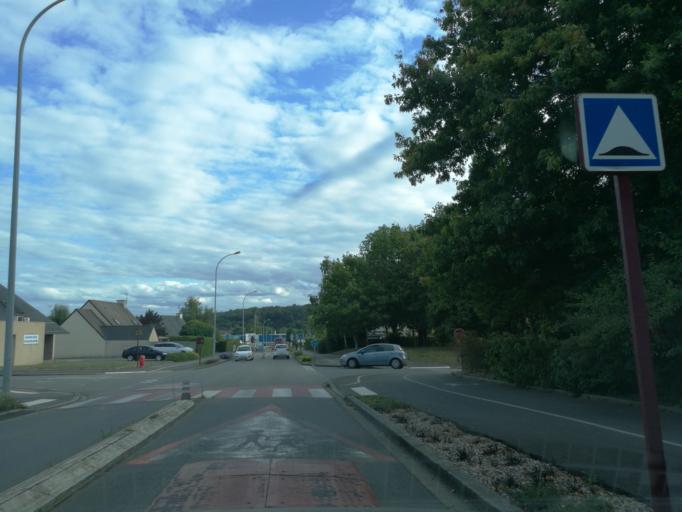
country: FR
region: Brittany
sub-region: Departement d'Ille-et-Vilaine
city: Montfort-sur-Meu
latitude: 48.1354
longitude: -1.9474
